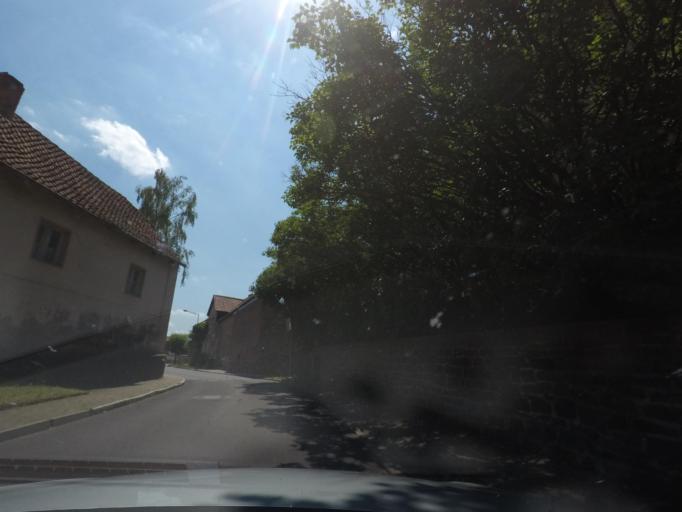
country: DE
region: Saxony-Anhalt
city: Haldensleben I
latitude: 52.2468
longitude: 11.3987
